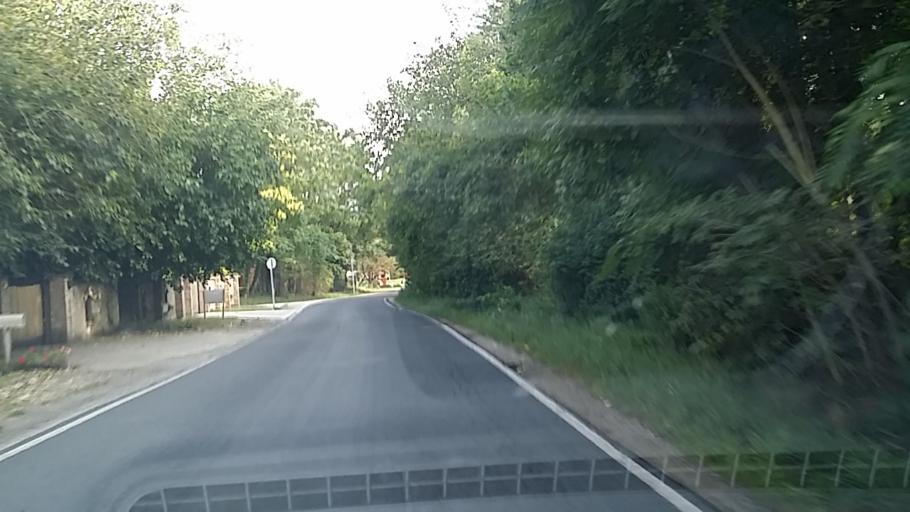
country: HU
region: Gyor-Moson-Sopron
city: Fertorakos
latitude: 47.7276
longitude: 16.6231
